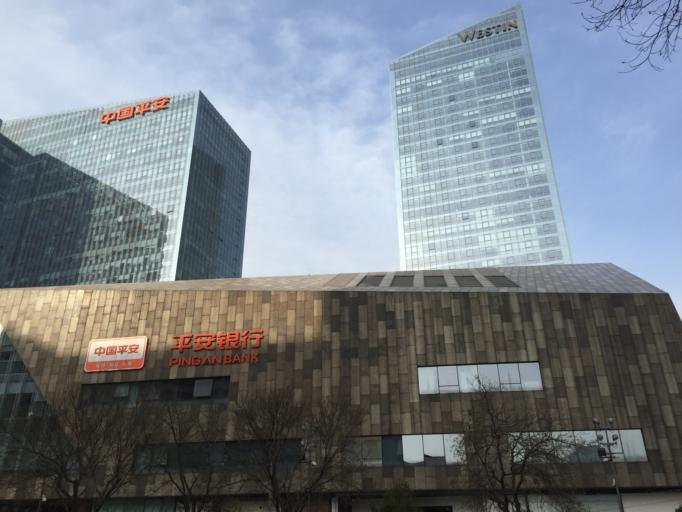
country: CN
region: Beijing
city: Chaowai
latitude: 39.9479
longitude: 116.4548
